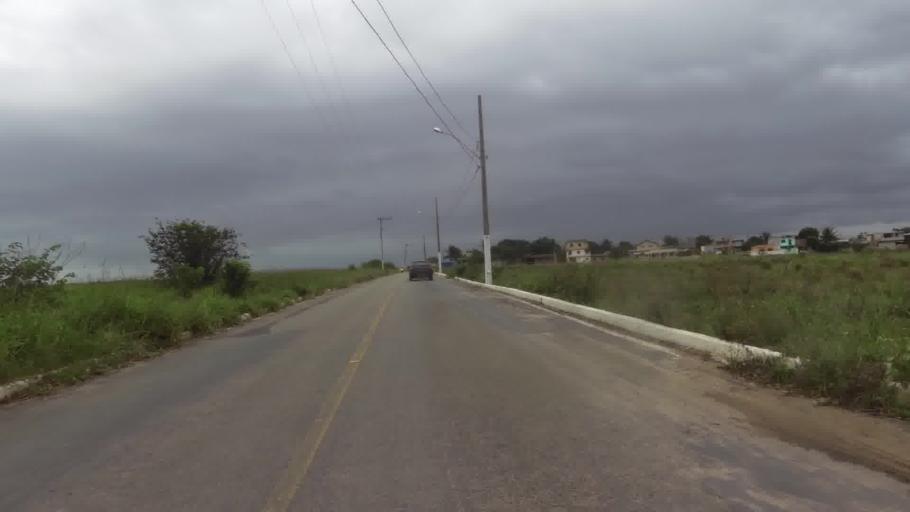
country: BR
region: Espirito Santo
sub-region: Marataizes
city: Marataizes
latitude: -21.0525
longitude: -40.8370
